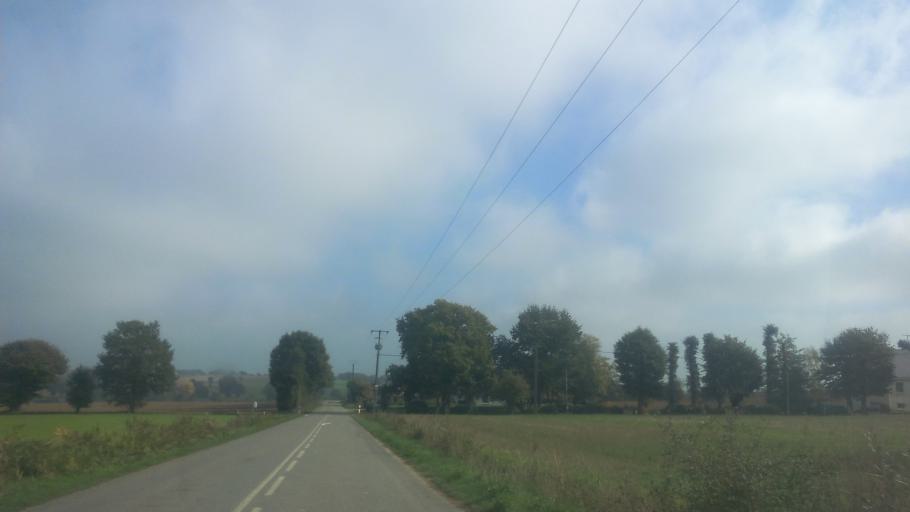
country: FR
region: Pays de la Loire
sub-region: Departement de la Loire-Atlantique
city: Conquereuil
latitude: 47.6262
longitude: -1.7785
